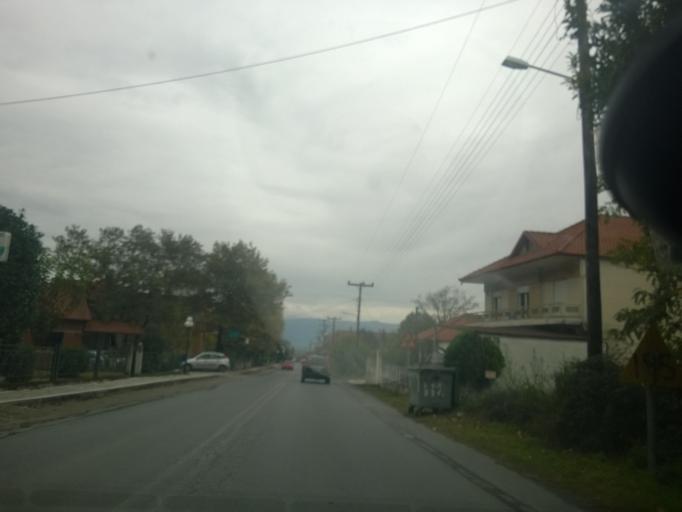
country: GR
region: Central Macedonia
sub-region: Nomos Pellis
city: Loutraki
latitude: 40.9693
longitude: 21.9436
